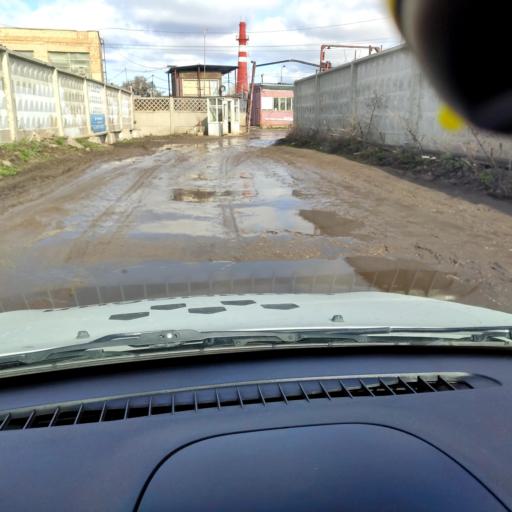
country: RU
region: Samara
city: Tol'yatti
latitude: 53.5613
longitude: 49.3183
